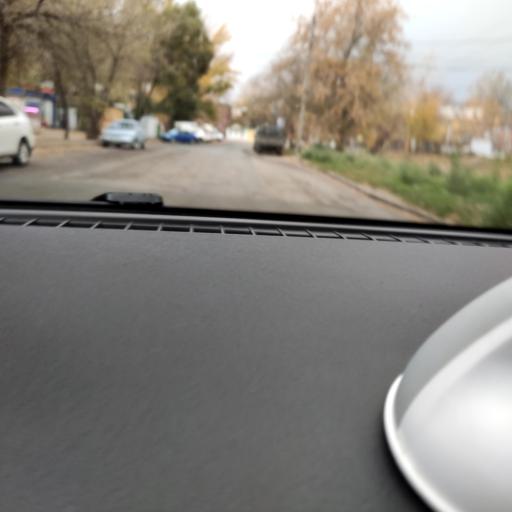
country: RU
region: Samara
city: Smyshlyayevka
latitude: 53.2279
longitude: 50.2985
